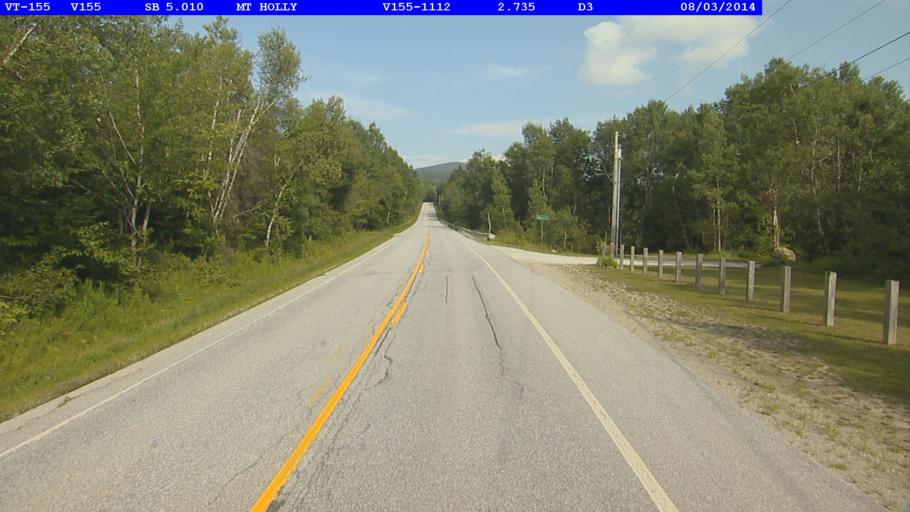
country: US
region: Vermont
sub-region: Windsor County
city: Chester
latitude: 43.3934
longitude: -72.8190
